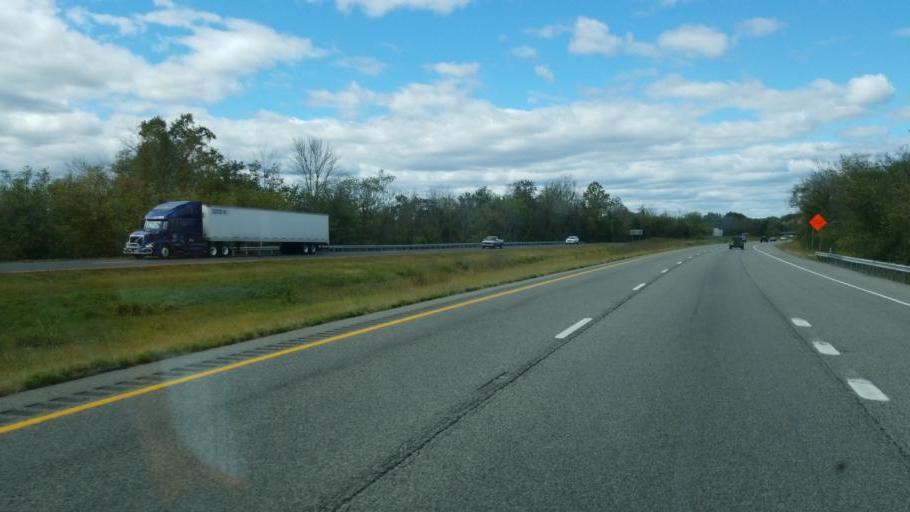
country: US
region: Maryland
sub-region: Washington County
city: Hancock
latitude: 39.6314
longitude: -78.0206
